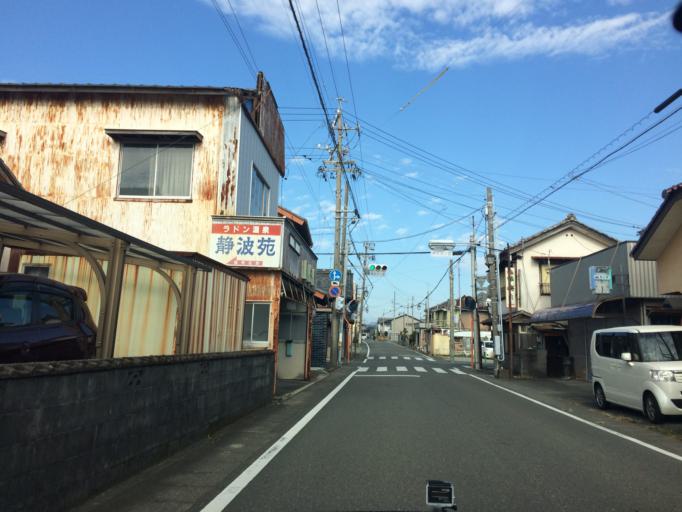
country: JP
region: Shizuoka
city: Sagara
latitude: 34.7354
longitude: 138.2226
